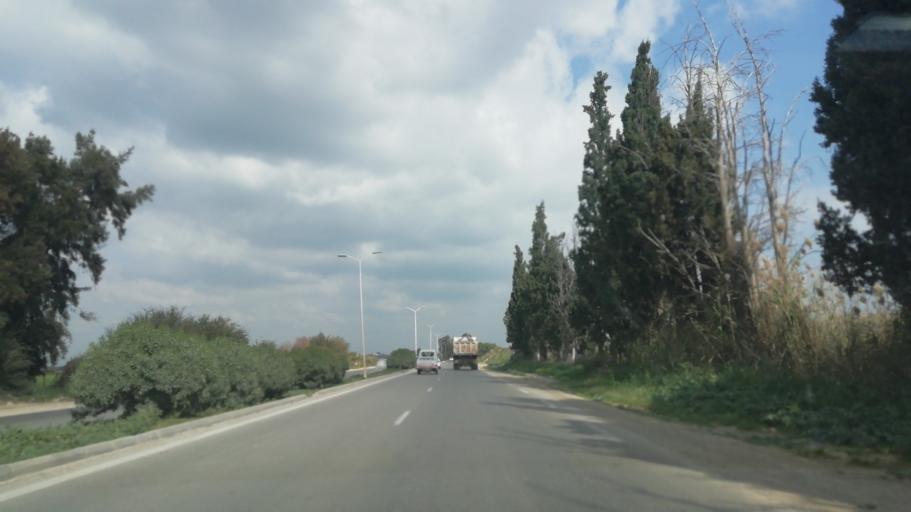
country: DZ
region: Mascara
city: Mascara
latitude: 35.6038
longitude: 0.0882
